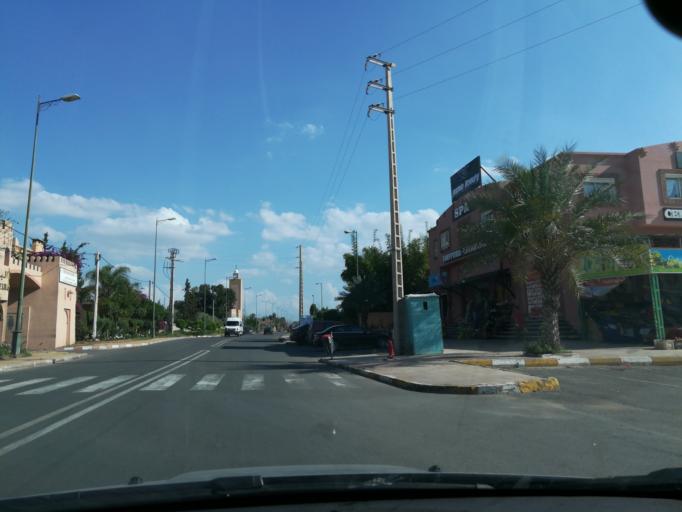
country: MA
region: Marrakech-Tensift-Al Haouz
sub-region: Marrakech
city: Marrakesh
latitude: 31.6616
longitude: -8.0550
